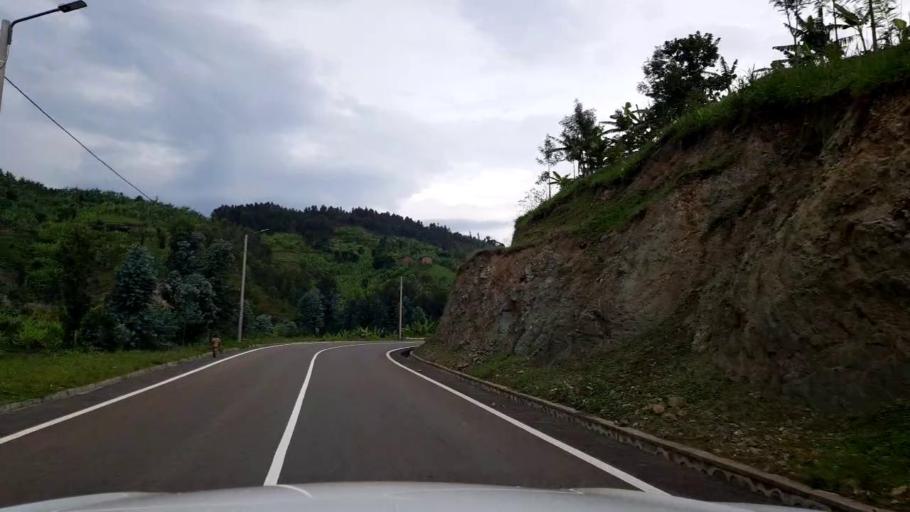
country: RW
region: Western Province
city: Kibuye
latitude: -2.0292
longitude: 29.3947
